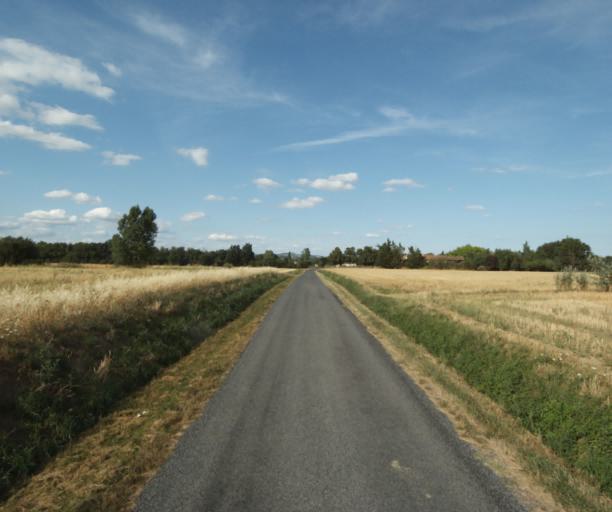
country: FR
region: Midi-Pyrenees
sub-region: Departement de la Haute-Garonne
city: Revel
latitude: 43.5021
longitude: 1.9795
